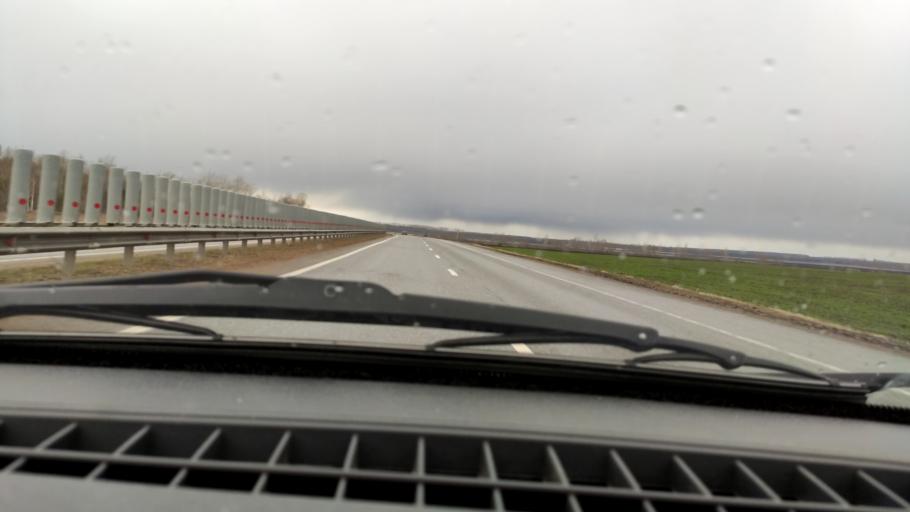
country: RU
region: Bashkortostan
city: Kushnarenkovo
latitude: 55.0657
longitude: 55.3661
